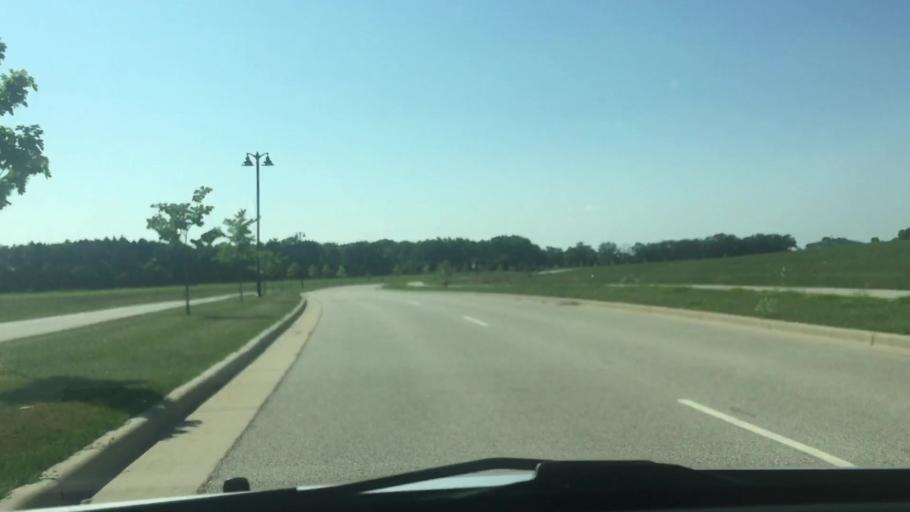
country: US
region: Wisconsin
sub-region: Waukesha County
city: Delafield
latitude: 43.0677
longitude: -88.4526
